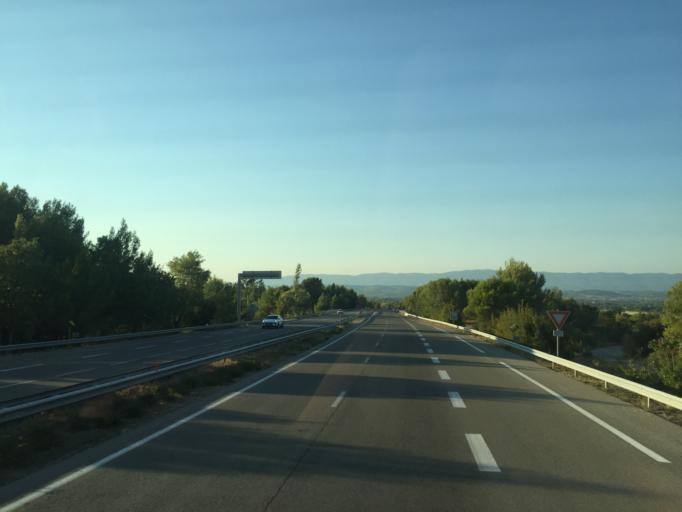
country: FR
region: Provence-Alpes-Cote d'Azur
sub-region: Departement des Bouches-du-Rhone
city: Meyrargues
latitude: 43.6354
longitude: 5.4943
